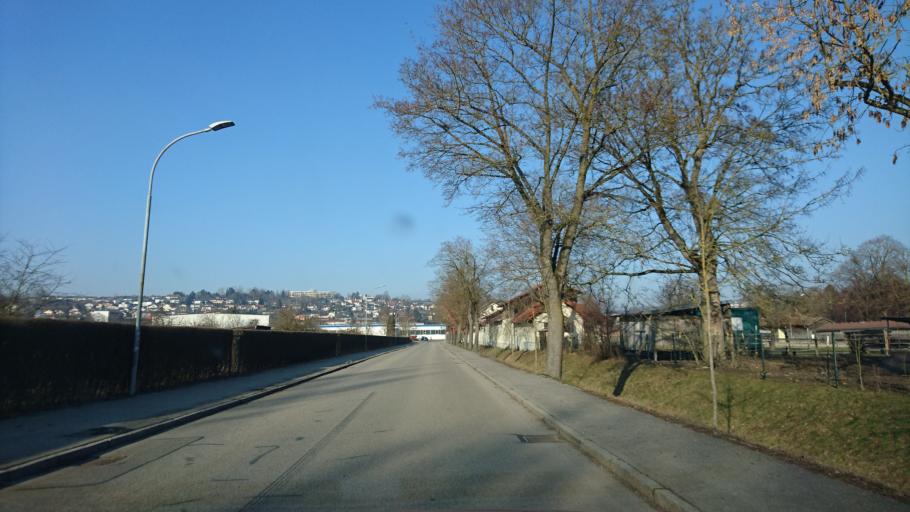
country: DE
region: Bavaria
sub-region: Lower Bavaria
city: Pfarrkirchen
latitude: 48.4259
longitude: 12.9302
